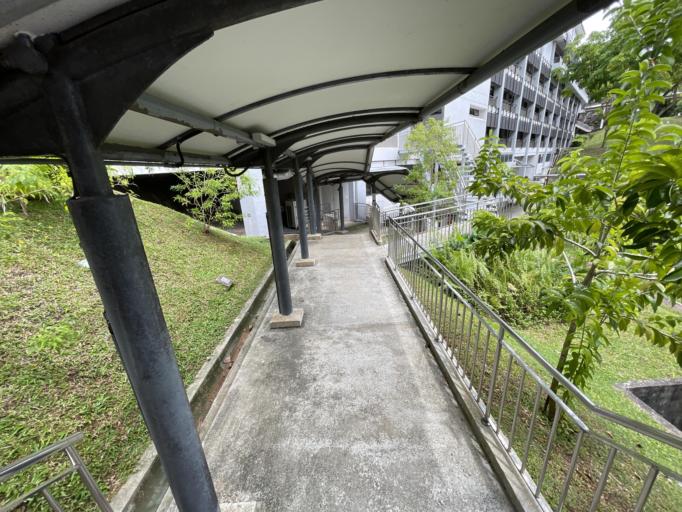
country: SG
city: Singapore
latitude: 1.2933
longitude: 103.7747
